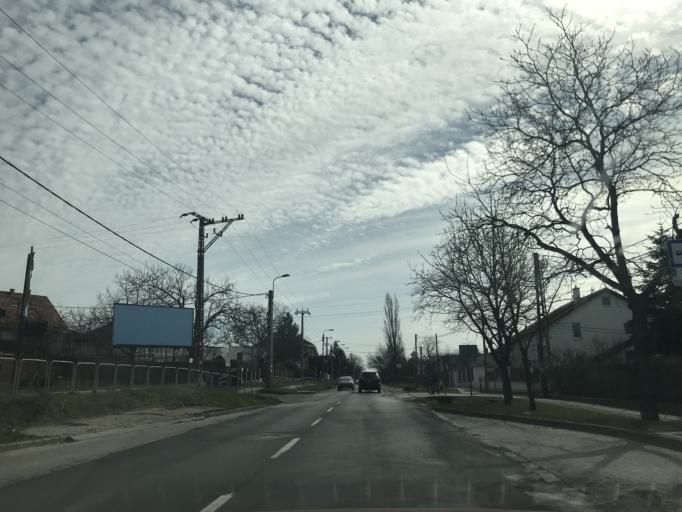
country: HU
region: Budapest
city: Budapest XVI. keruelet
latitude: 47.5346
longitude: 19.1820
